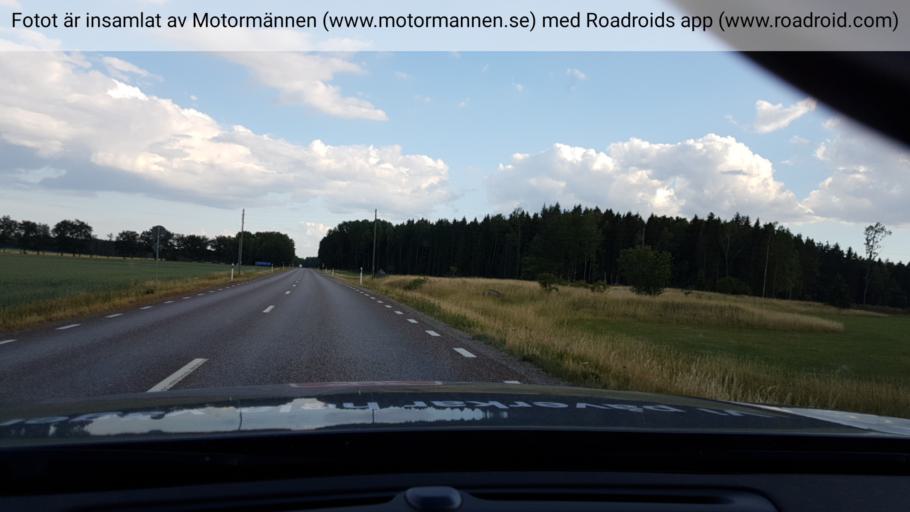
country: SE
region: Uppsala
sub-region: Enkopings Kommun
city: Irsta
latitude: 59.7972
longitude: 16.9008
